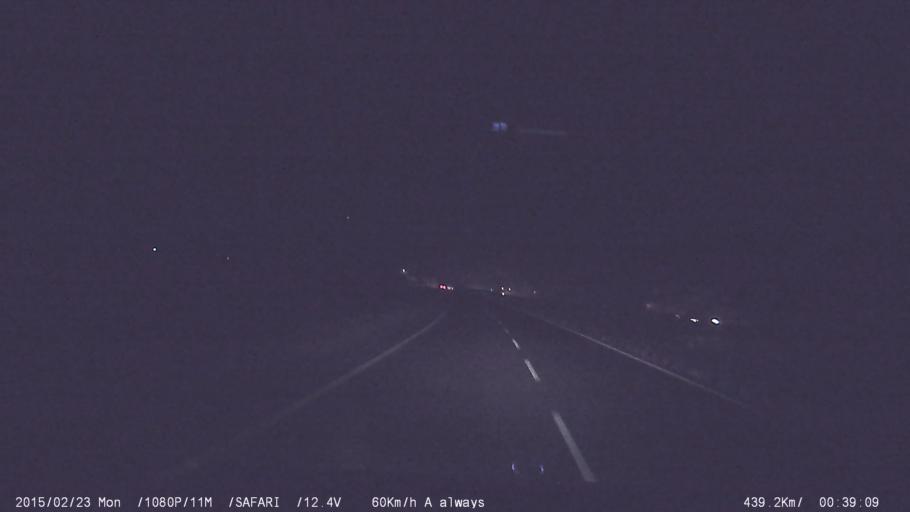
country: IN
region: Tamil Nadu
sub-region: Dharmapuri
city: Dharmapuri
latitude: 12.0085
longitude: 78.0823
